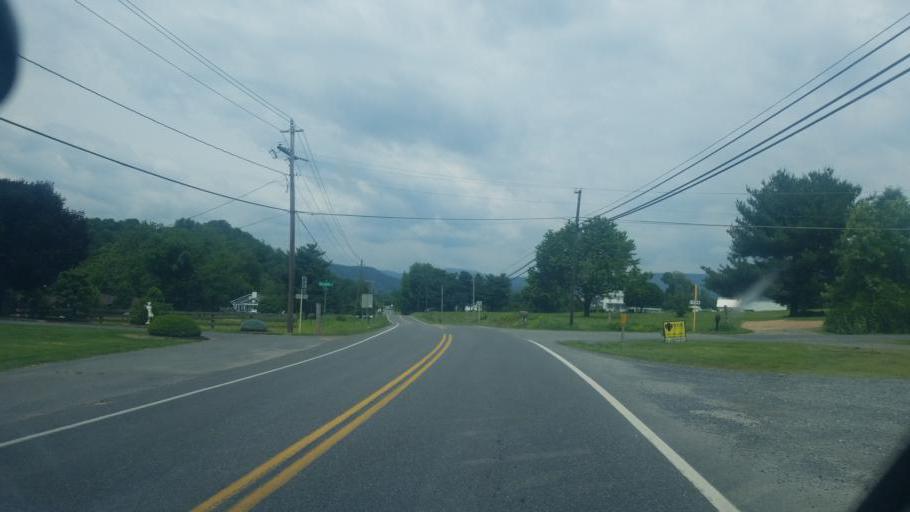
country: US
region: Virginia
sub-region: Rockingham County
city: Dayton
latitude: 38.4711
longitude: -78.9792
